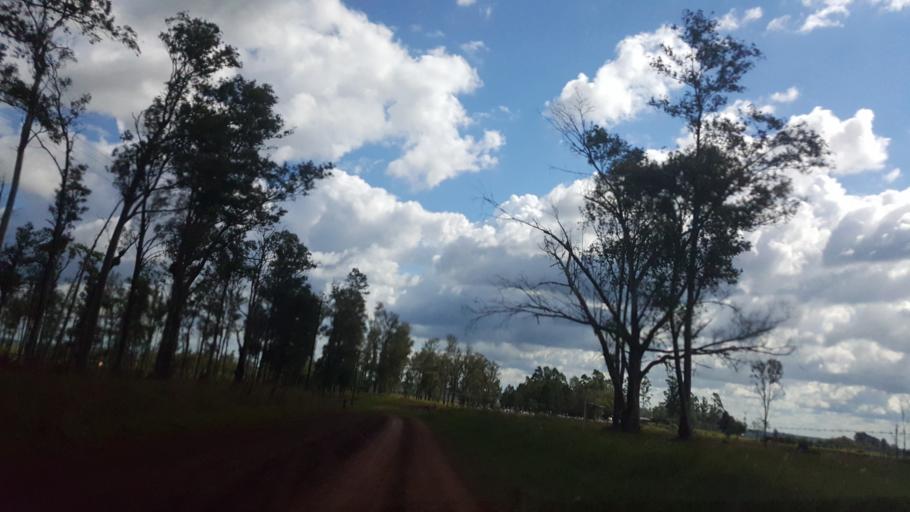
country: AR
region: Misiones
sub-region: Departamento de Capital
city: Posadas
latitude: -27.4184
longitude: -56.0032
